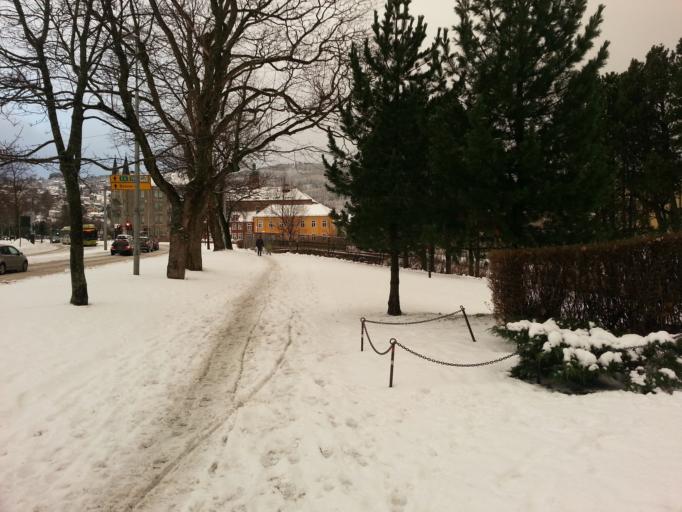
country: NO
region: Sor-Trondelag
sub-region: Trondheim
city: Trondheim
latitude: 63.4304
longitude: 10.3764
